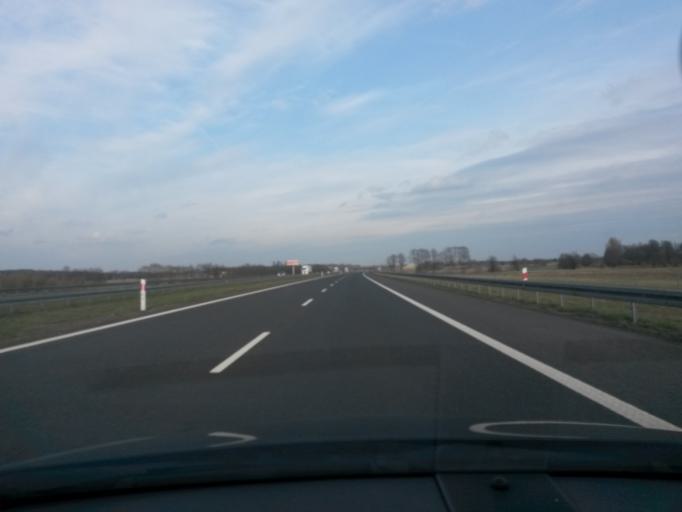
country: PL
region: Lodz Voivodeship
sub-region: Powiat zgierski
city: Parzeczew
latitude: 51.9397
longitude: 19.2251
